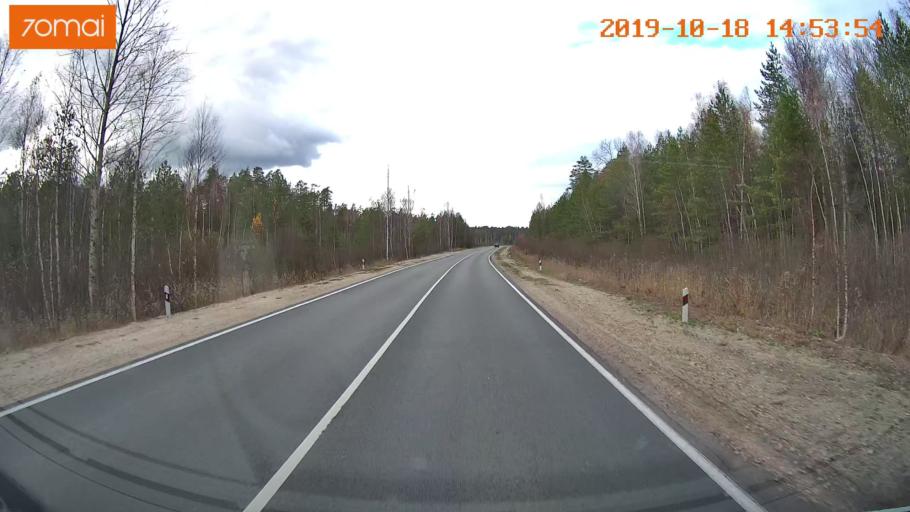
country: RU
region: Vladimir
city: Kurlovo
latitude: 55.4350
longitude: 40.6083
